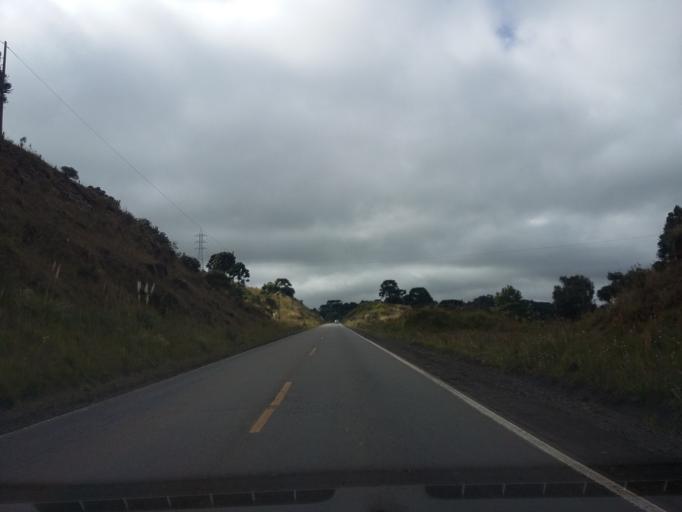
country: BR
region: Santa Catarina
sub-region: Lages
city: Lages
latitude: -27.8868
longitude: -50.1627
